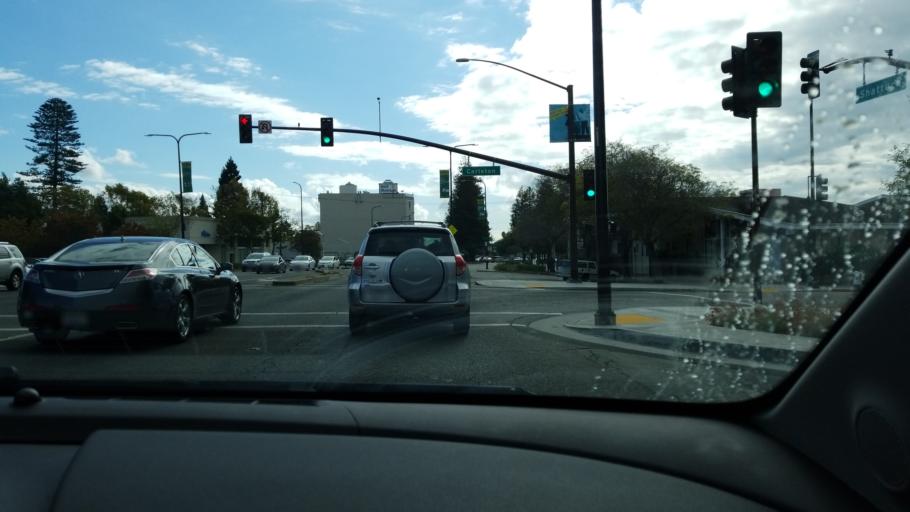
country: US
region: California
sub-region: Alameda County
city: Berkeley
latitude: 37.8614
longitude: -122.2672
